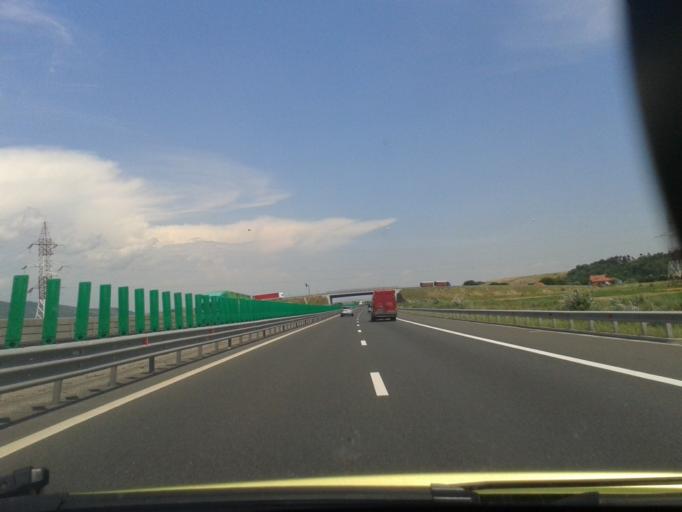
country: RO
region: Alba
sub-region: Comuna Sibot
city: Sibot
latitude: 45.9209
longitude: 23.3366
